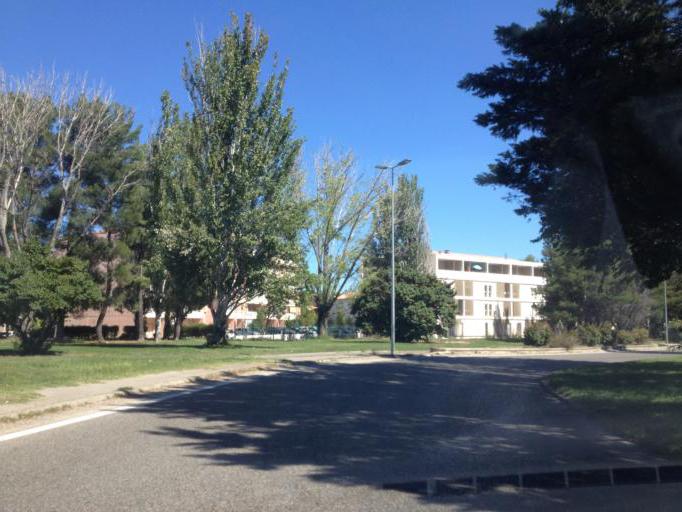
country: FR
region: Provence-Alpes-Cote d'Azur
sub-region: Departement des Bouches-du-Rhone
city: Aix-en-Provence
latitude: 43.5304
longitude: 5.4172
